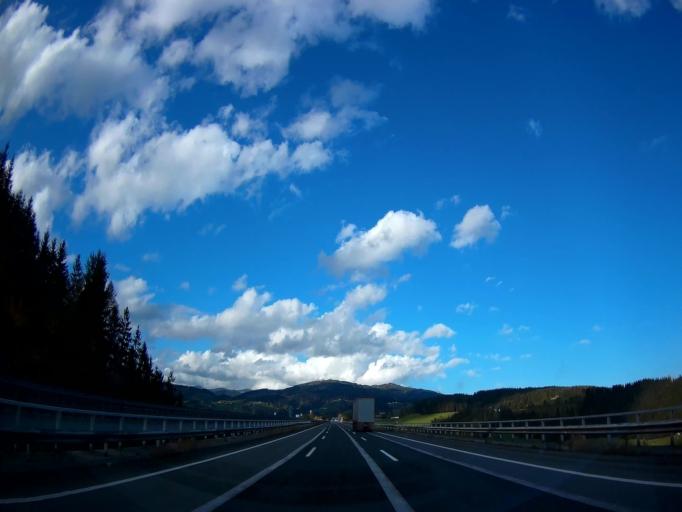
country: AT
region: Carinthia
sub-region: Politischer Bezirk Wolfsberg
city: Bad Sankt Leonhard im Lavanttal
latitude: 46.9174
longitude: 14.8389
